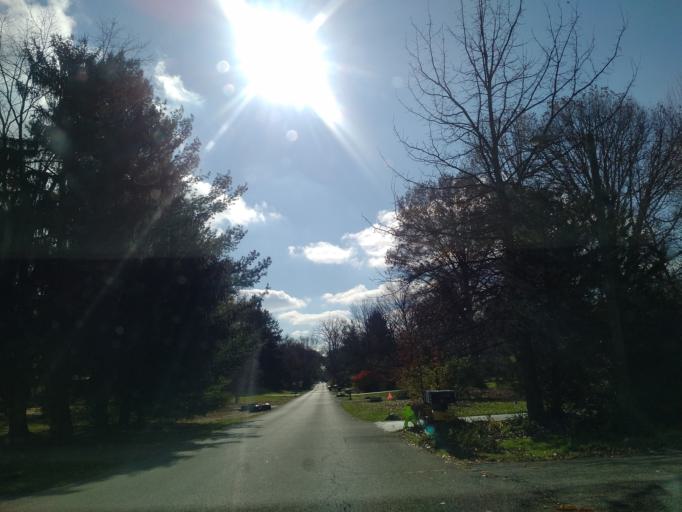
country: US
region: Indiana
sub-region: Marion County
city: Meridian Hills
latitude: 39.9173
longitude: -86.1233
